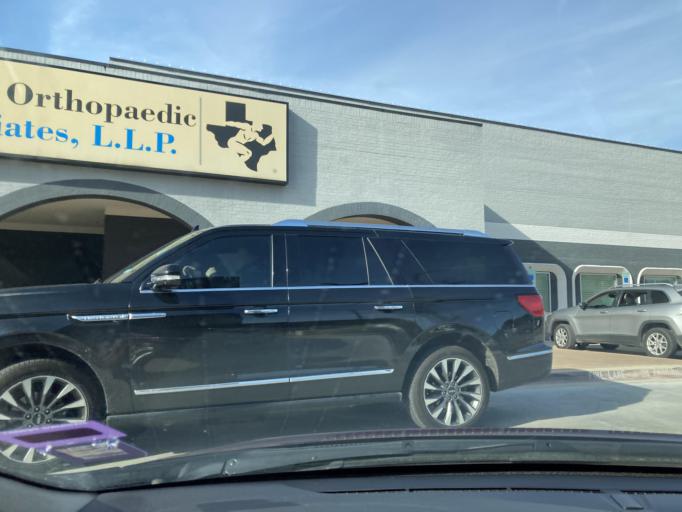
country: US
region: Texas
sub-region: Dallas County
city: University Park
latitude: 32.8818
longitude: -96.7671
